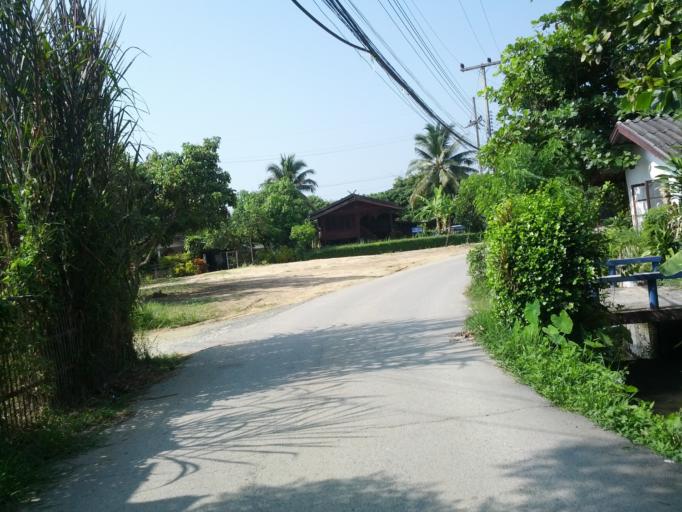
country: TH
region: Chiang Mai
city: San Kamphaeng
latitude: 18.7824
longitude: 99.1008
